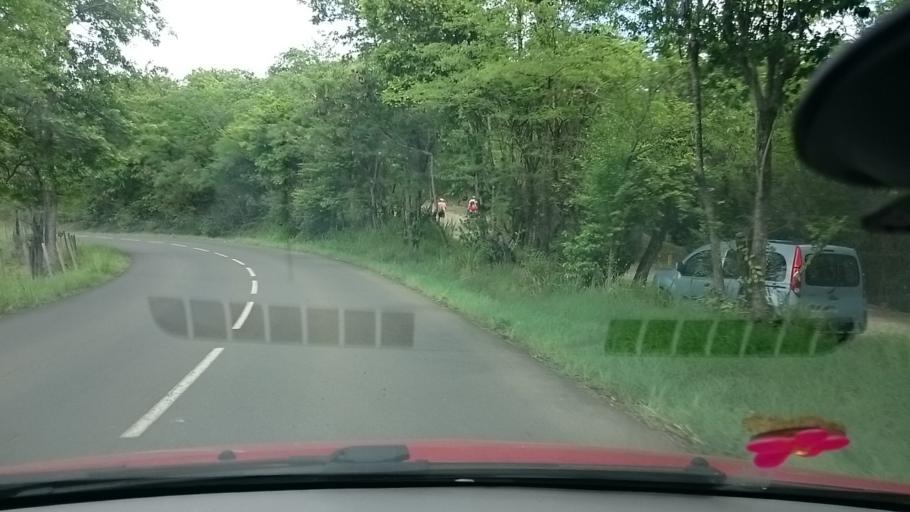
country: MQ
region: Martinique
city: Petite Riviere Salee
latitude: 14.7574
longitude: -60.9327
